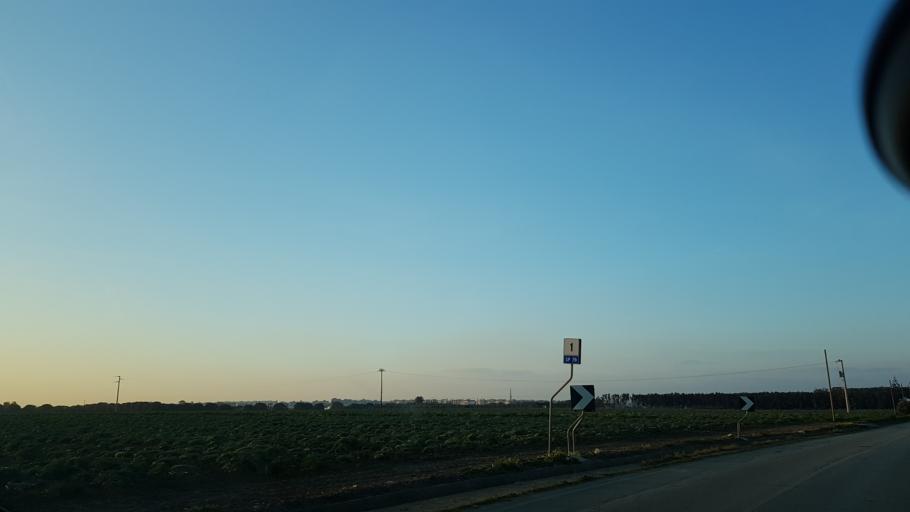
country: IT
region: Apulia
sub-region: Provincia di Brindisi
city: La Rosa
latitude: 40.6064
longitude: 17.9449
